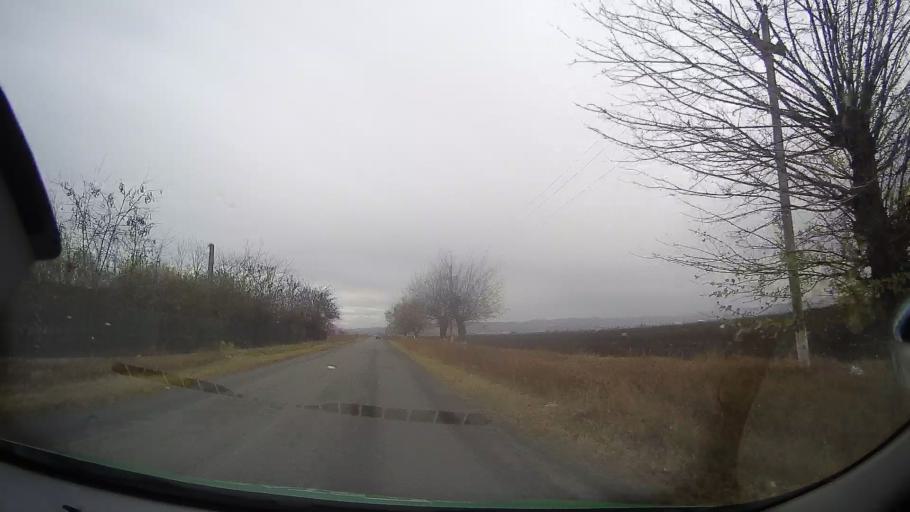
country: RO
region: Prahova
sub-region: Comuna Colceag
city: Inotesti
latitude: 44.9738
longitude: 26.3422
